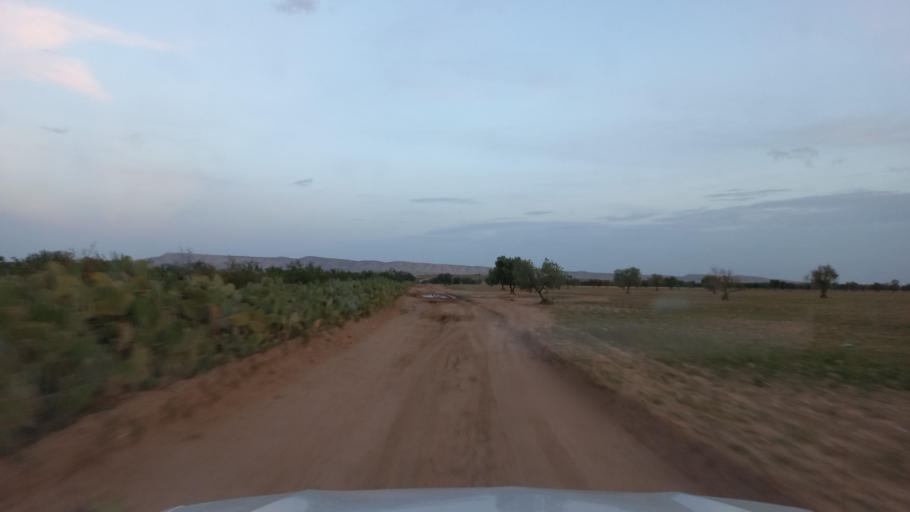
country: TN
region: Al Qasrayn
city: Sbiba
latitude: 35.3484
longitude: 9.0498
